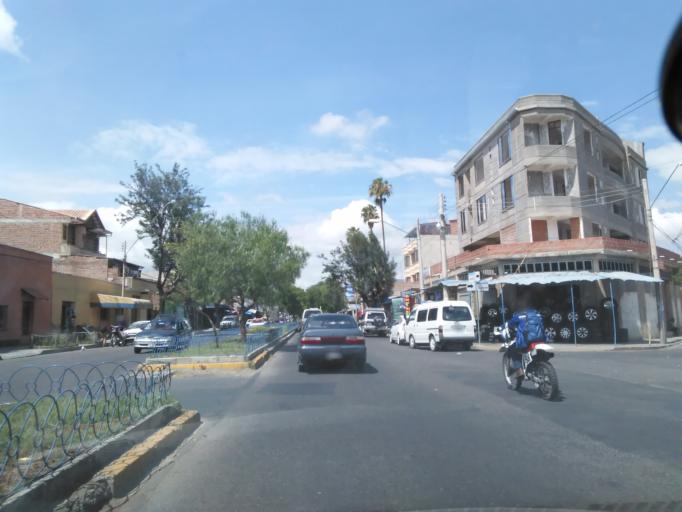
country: BO
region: Cochabamba
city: Cochabamba
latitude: -17.4070
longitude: -66.1639
